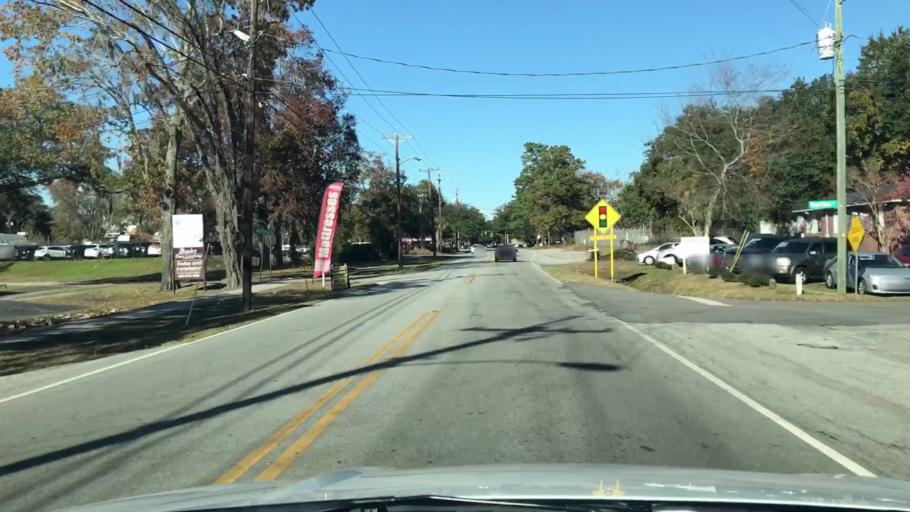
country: US
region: South Carolina
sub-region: Charleston County
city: North Charleston
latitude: 32.7977
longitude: -80.0158
